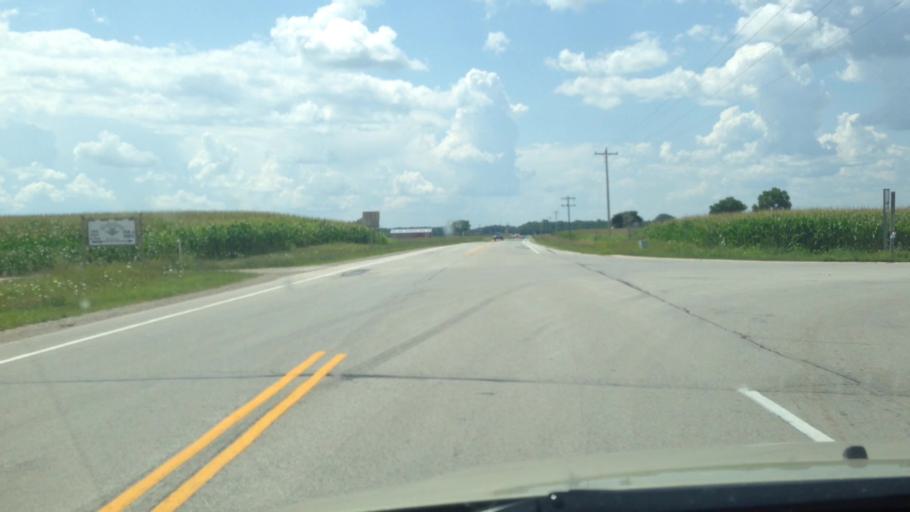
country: US
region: Wisconsin
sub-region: Brown County
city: Pulaski
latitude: 44.6465
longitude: -88.1500
